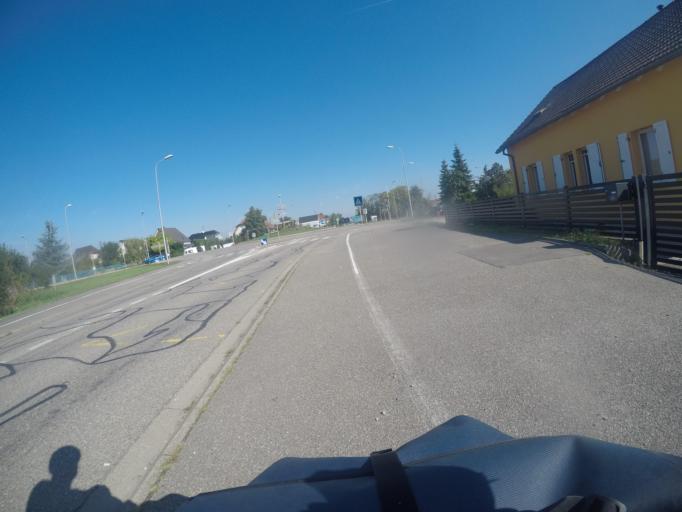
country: FR
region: Alsace
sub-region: Departement du Haut-Rhin
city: Bantzenheim
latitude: 47.8135
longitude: 7.5062
